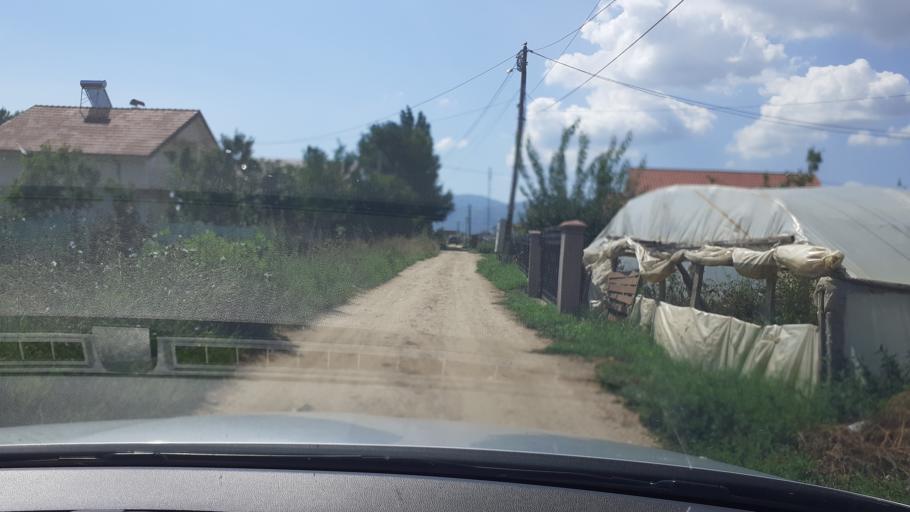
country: MK
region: Vasilevo
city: Vasilevo
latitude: 41.4698
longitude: 22.6423
